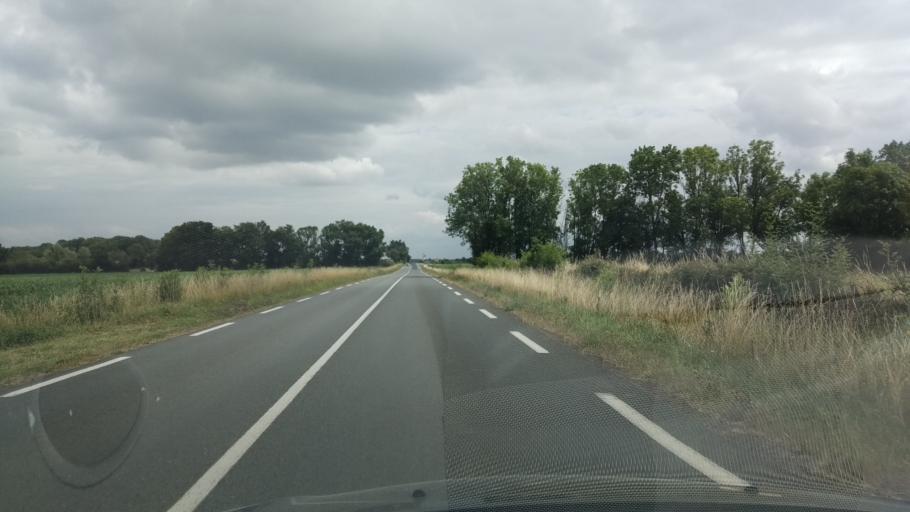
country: FR
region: Poitou-Charentes
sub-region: Departement de la Vienne
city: Saint-Maurice-la-Clouere
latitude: 46.3935
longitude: 0.3989
